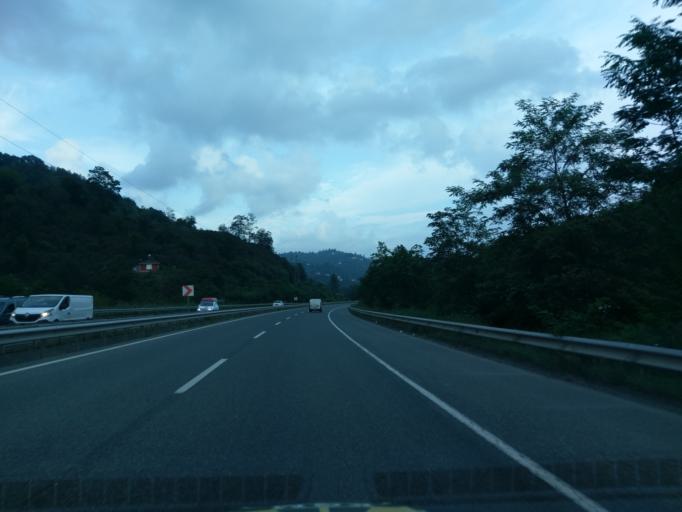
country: TR
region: Ordu
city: Bolaman
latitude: 41.0230
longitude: 37.5984
